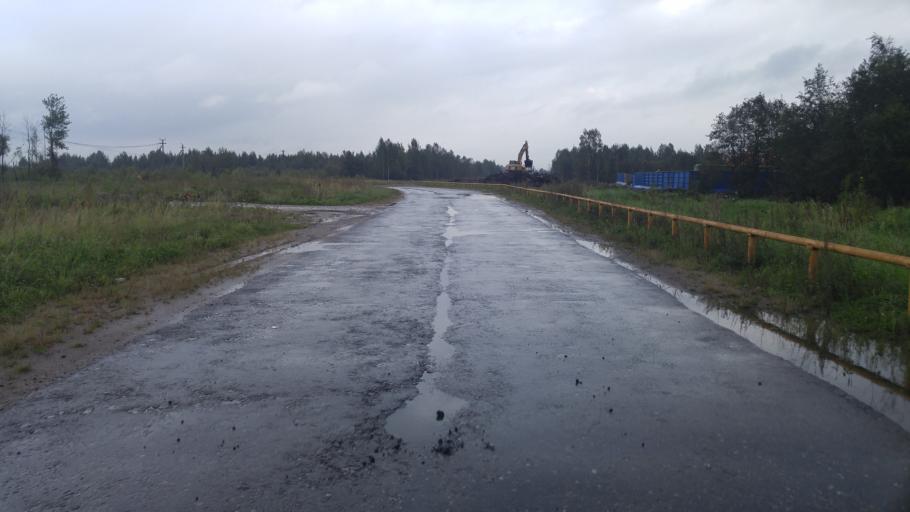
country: RU
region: St.-Petersburg
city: Ust'-Izhora
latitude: 59.7845
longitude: 30.5748
